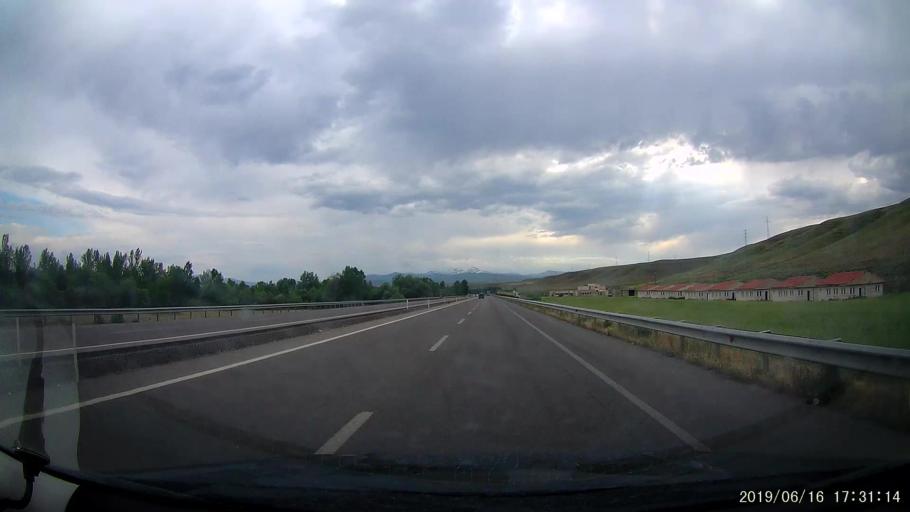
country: TR
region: Erzincan
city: Tercan
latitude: 39.7743
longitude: 40.3283
